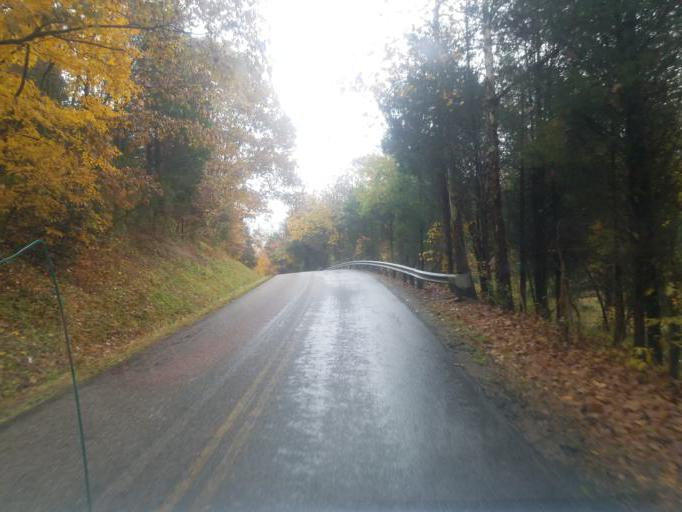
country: US
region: Ohio
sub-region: Washington County
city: Beverly
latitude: 39.5504
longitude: -81.6681
